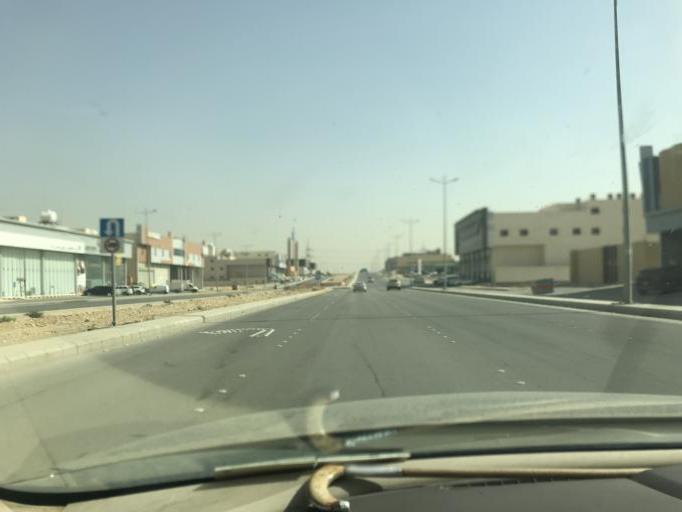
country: SA
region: Ar Riyad
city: Riyadh
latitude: 24.8231
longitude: 46.7285
